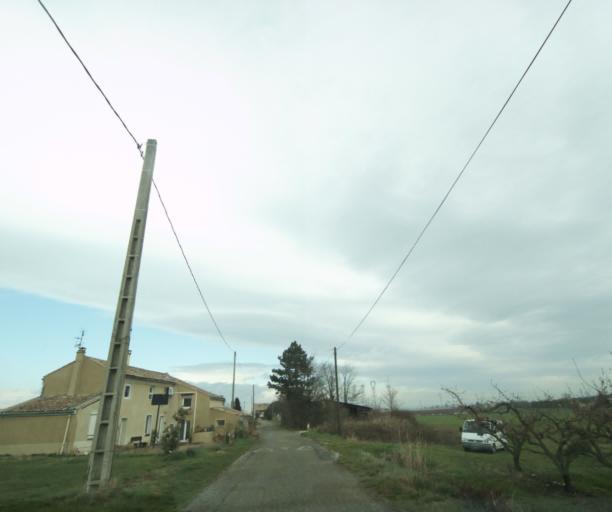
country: FR
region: Rhone-Alpes
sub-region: Departement de l'Ardeche
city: Cornas
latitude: 44.9774
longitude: 4.8760
